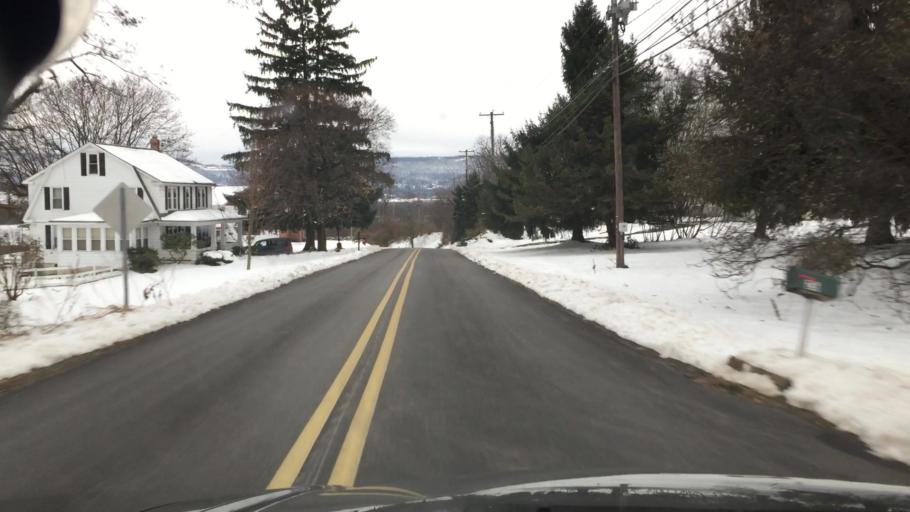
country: US
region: Pennsylvania
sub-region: Luzerne County
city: Conyngham
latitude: 41.0227
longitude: -76.0808
